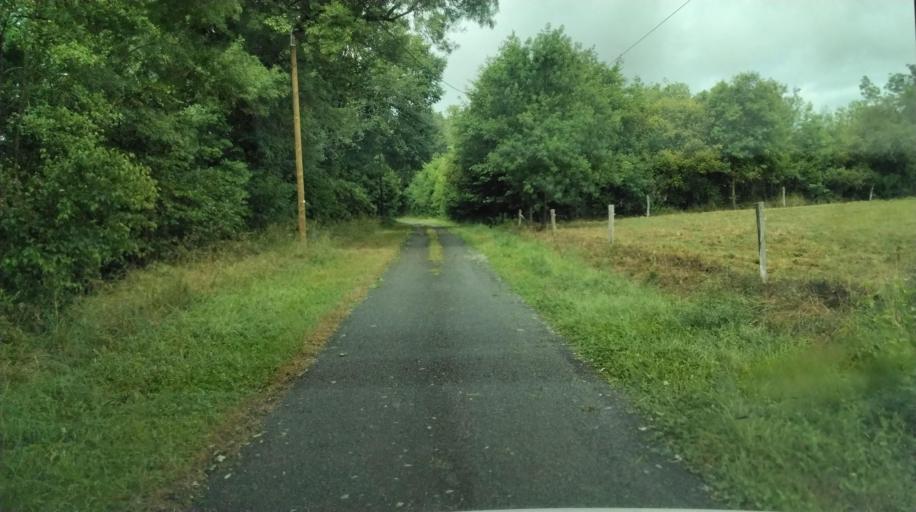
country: FR
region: Midi-Pyrenees
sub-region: Departement de la Haute-Garonne
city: Rieumes
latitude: 43.4224
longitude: 1.1597
